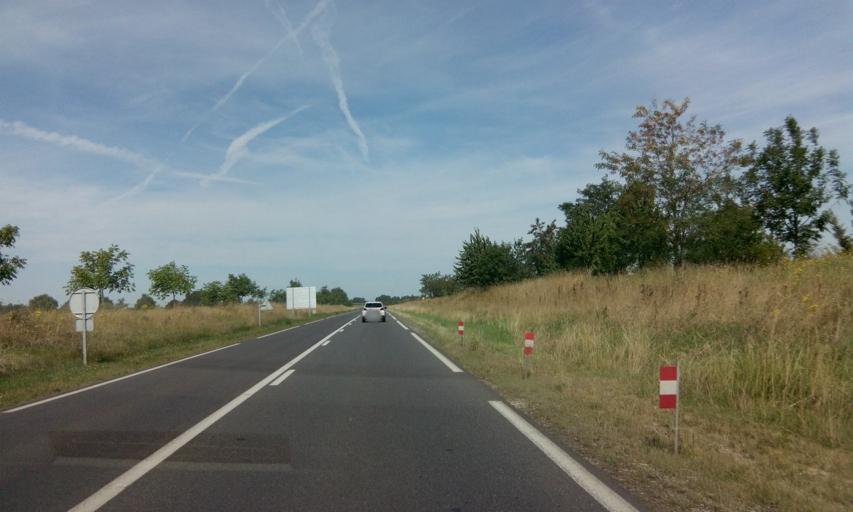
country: FR
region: Poitou-Charentes
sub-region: Departement de la Vienne
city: Charroux
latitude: 46.1508
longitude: 0.4051
